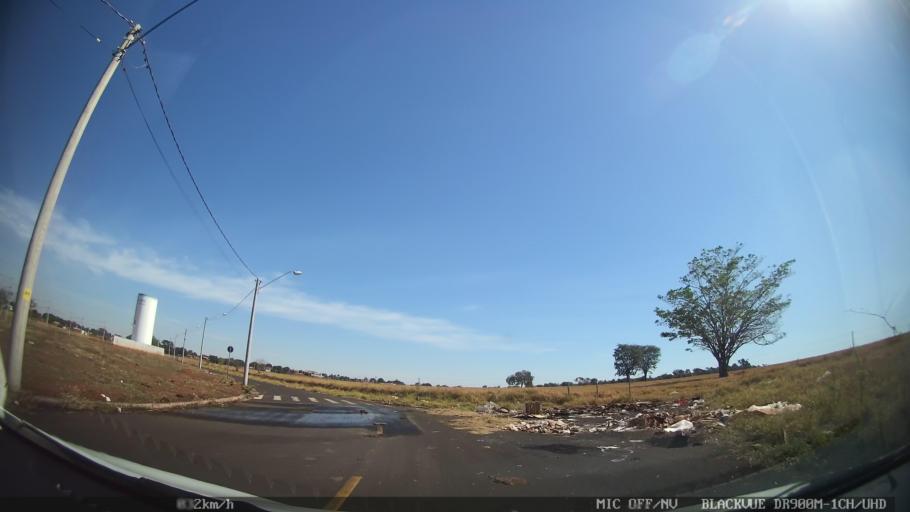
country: BR
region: Sao Paulo
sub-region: Sao Jose Do Rio Preto
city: Sao Jose do Rio Preto
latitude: -20.7480
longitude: -49.4247
